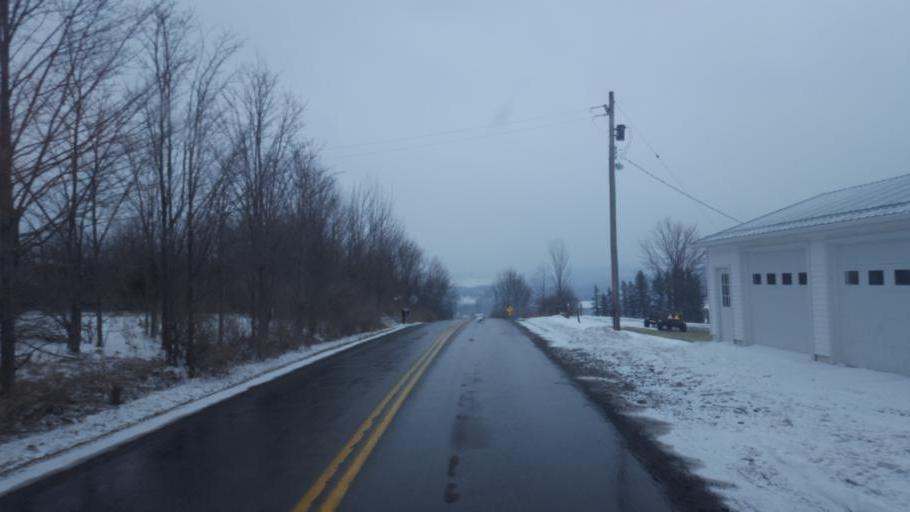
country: US
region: Pennsylvania
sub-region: Tioga County
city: Elkland
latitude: 42.0796
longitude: -77.4269
